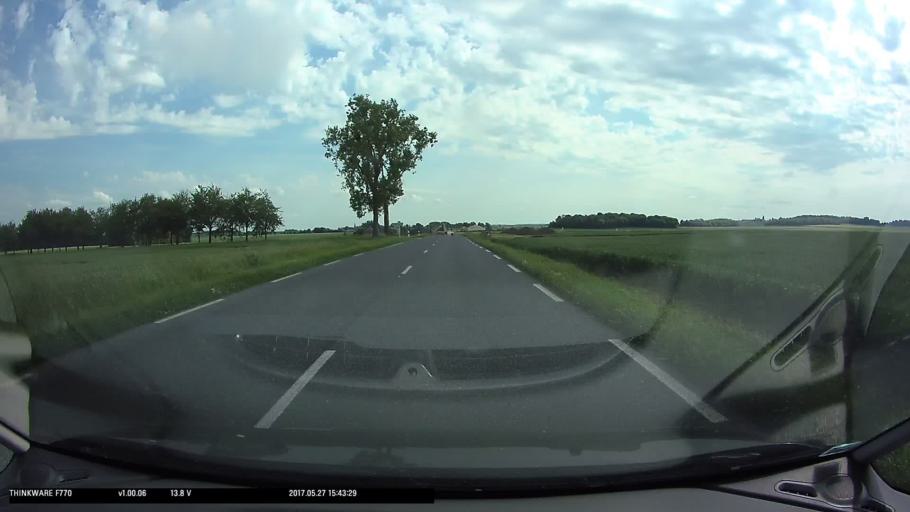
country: FR
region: Picardie
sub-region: Departement de l'Oise
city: Chaumont-en-Vexin
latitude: 49.2036
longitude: 1.8807
